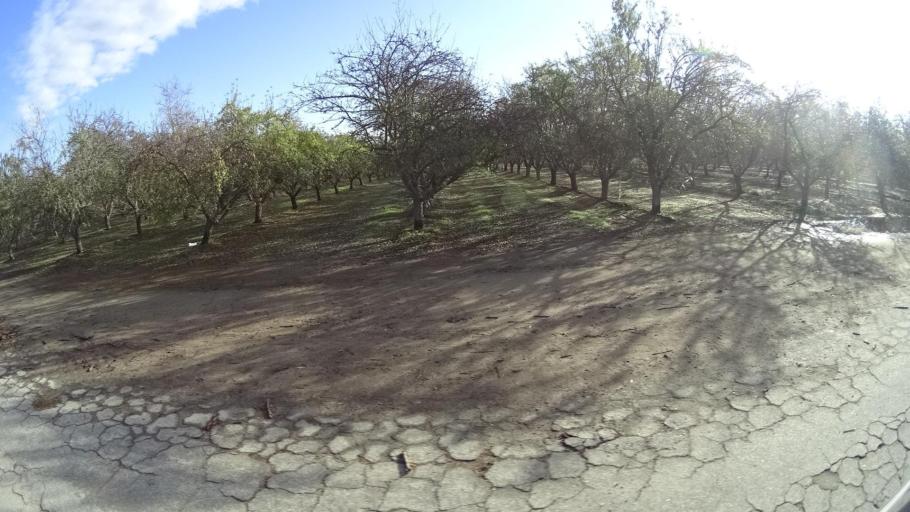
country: US
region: California
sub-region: Kern County
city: Delano
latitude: 35.7096
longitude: -119.3208
